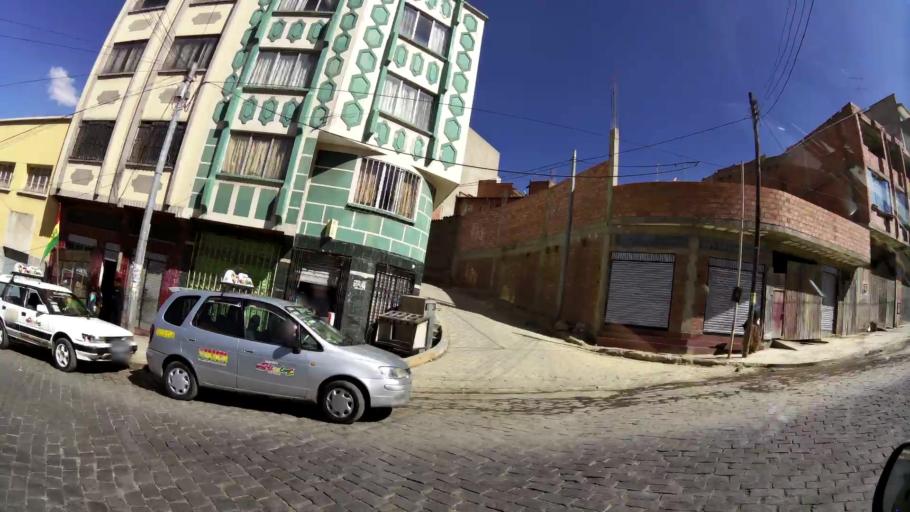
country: BO
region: La Paz
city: La Paz
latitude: -16.4935
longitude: -68.1590
